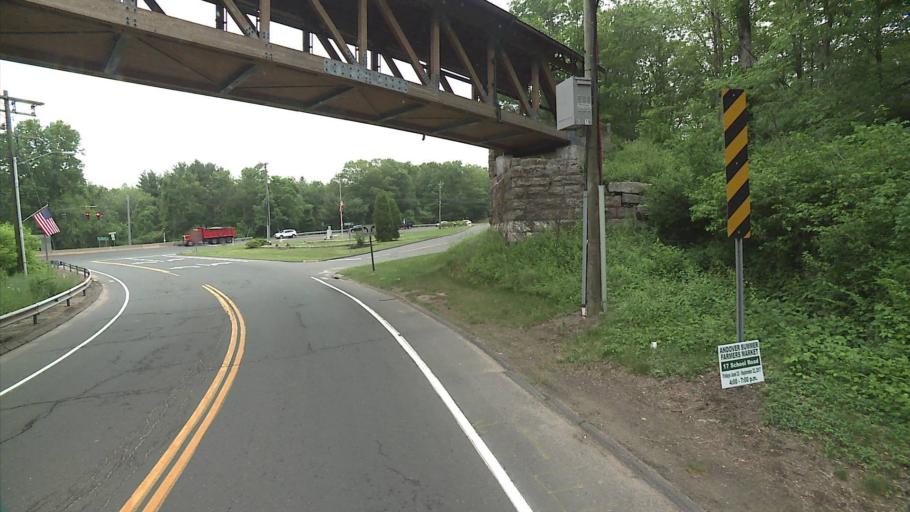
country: US
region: Connecticut
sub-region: Tolland County
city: Coventry Lake
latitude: 41.7378
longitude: -72.3686
